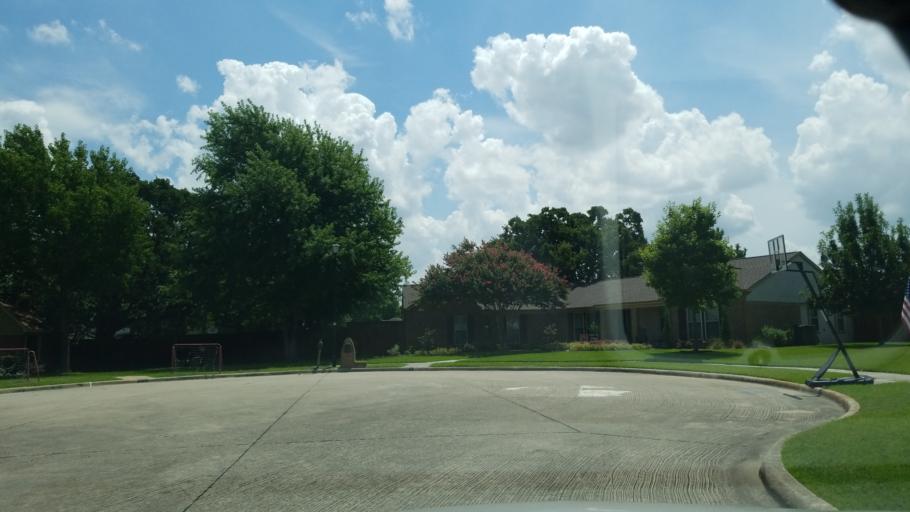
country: US
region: Texas
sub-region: Dallas County
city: Coppell
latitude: 32.9663
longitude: -96.9651
